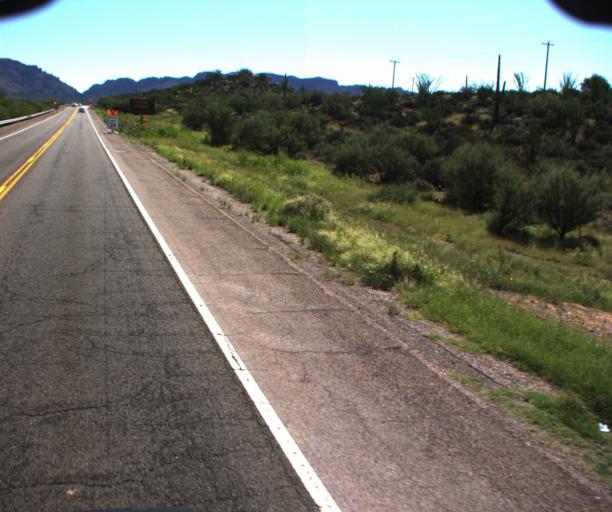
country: US
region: Arizona
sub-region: Pinal County
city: Superior
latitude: 33.2829
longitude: -111.1487
